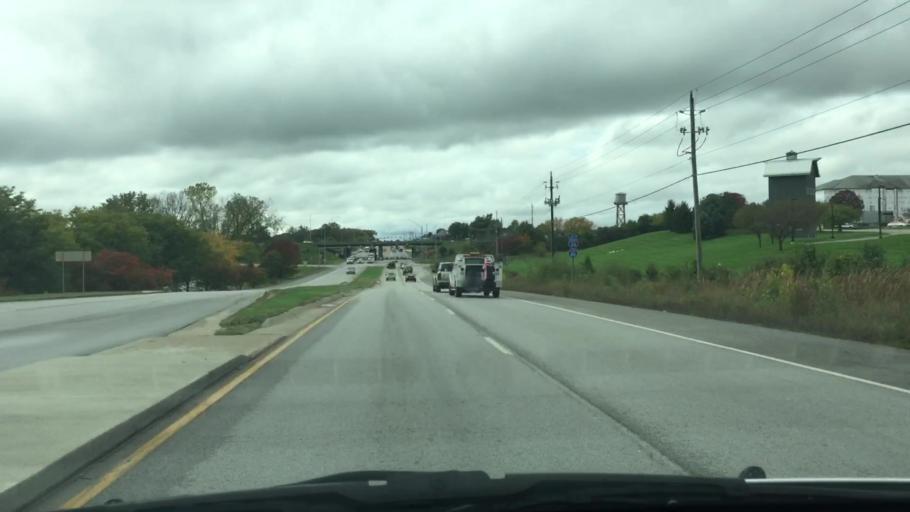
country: US
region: Iowa
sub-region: Polk County
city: Clive
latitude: 41.6150
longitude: -93.7720
